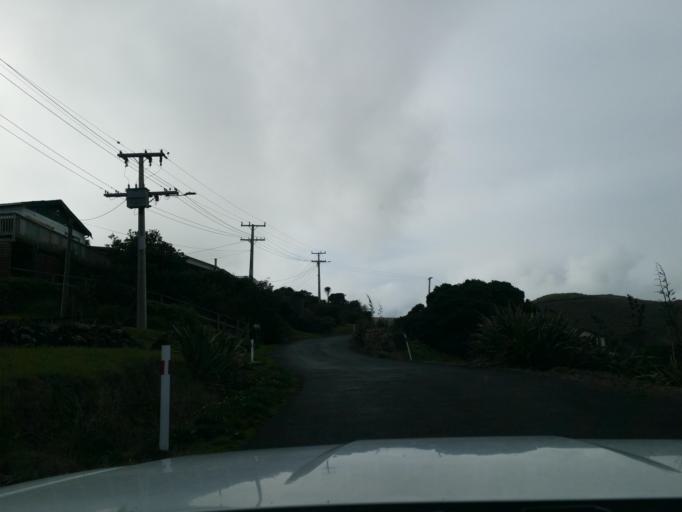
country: NZ
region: Northland
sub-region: Kaipara District
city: Dargaville
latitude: -35.7697
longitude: 173.5747
